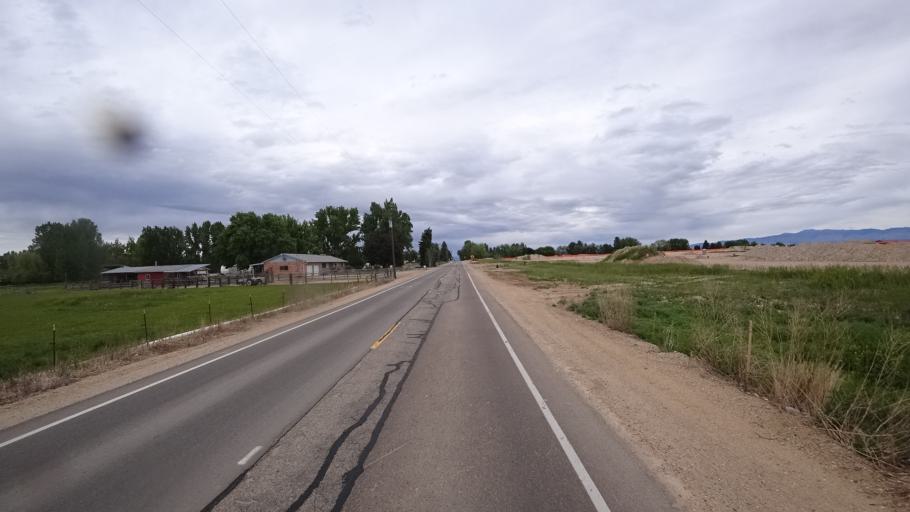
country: US
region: Idaho
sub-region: Ada County
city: Meridian
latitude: 43.5724
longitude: -116.4140
